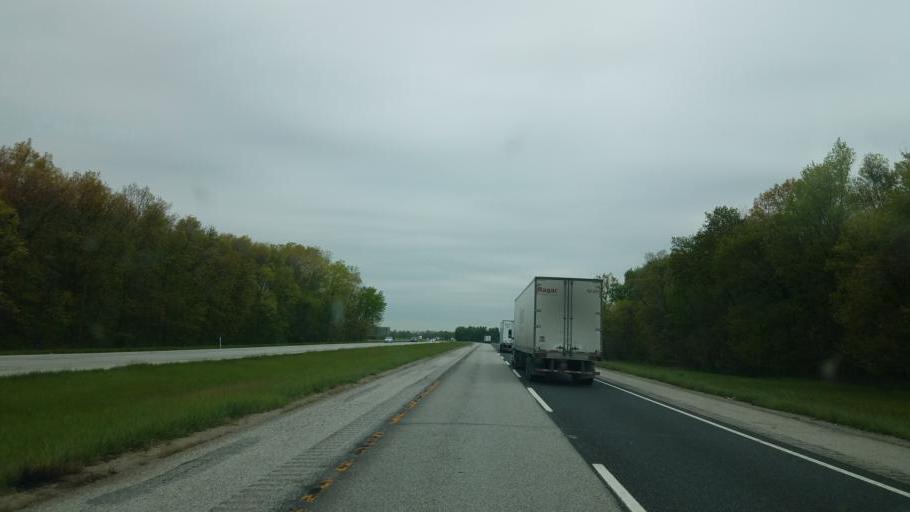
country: US
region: Michigan
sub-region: Saint Joseph County
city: Sturgis
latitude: 41.7535
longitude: -85.4679
